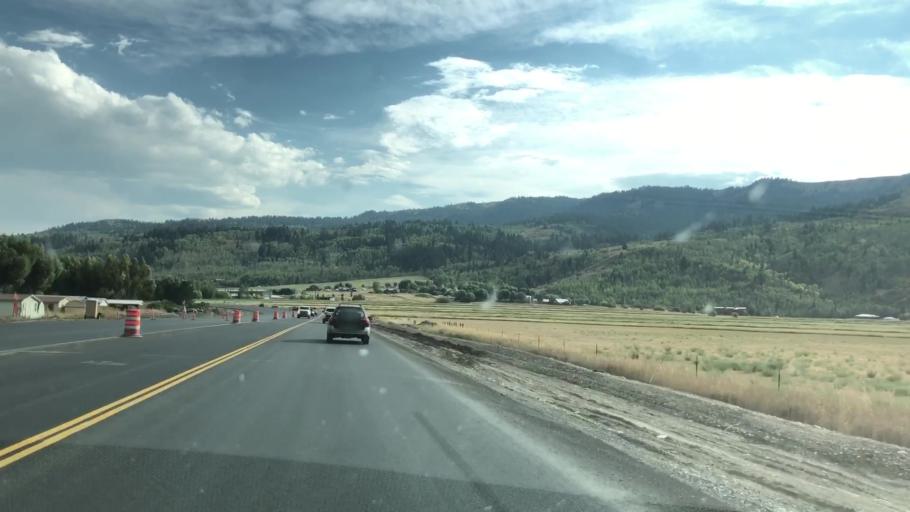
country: US
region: Wyoming
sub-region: Teton County
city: South Park
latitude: 43.3799
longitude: -110.7444
